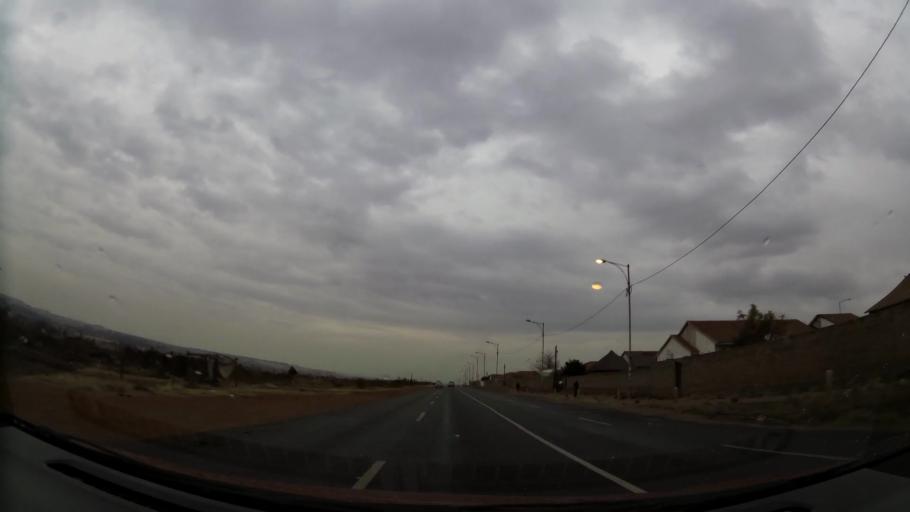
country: ZA
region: Gauteng
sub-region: City of Johannesburg Metropolitan Municipality
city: Roodepoort
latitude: -26.1662
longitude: 27.8066
